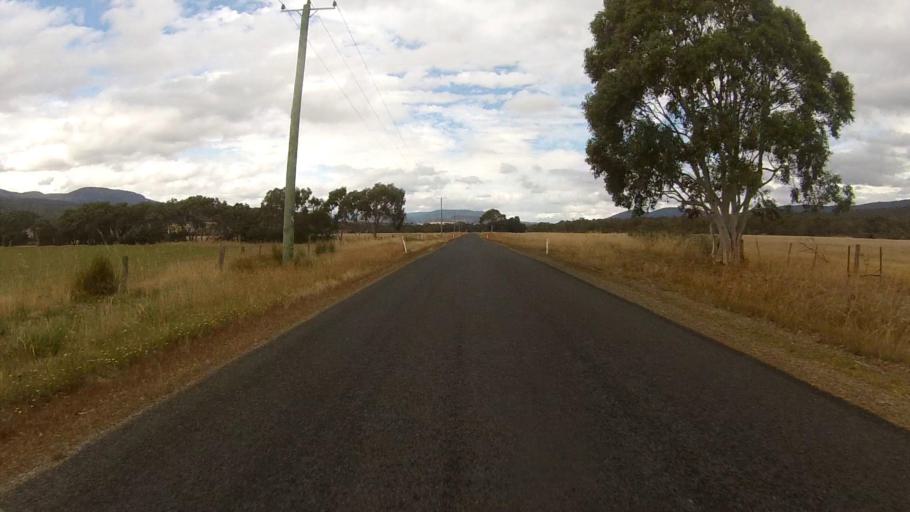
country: AU
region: Tasmania
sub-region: Break O'Day
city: St Helens
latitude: -41.8225
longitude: 147.8776
